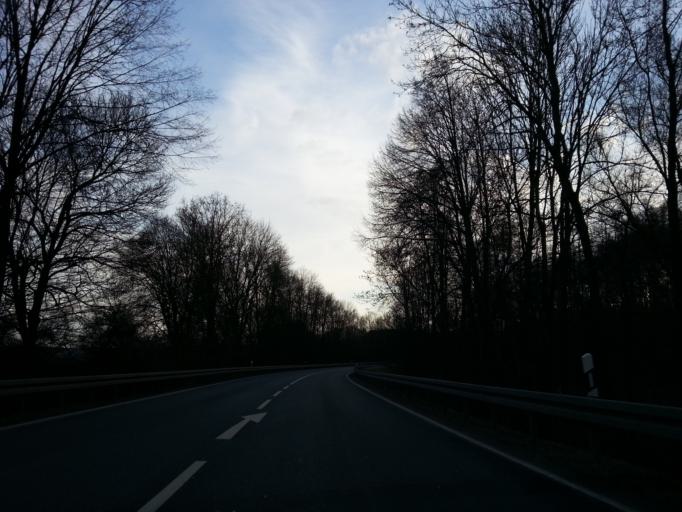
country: DE
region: Bavaria
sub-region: Regierungsbezirk Unterfranken
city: Waldbrunn
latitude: 49.7700
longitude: 9.7758
